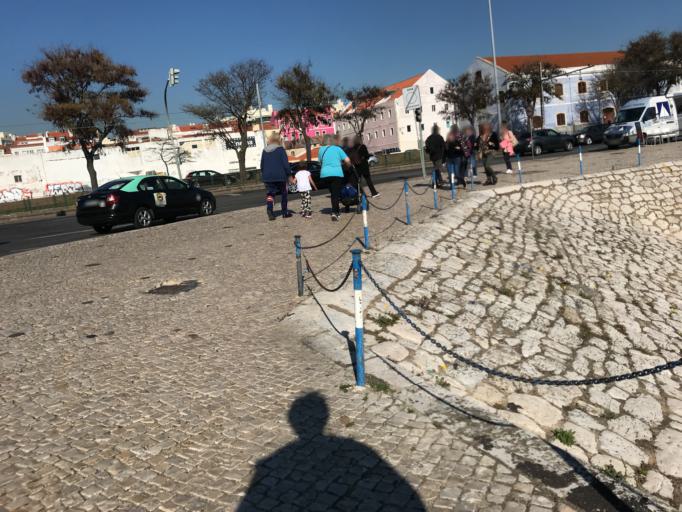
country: PT
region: Lisbon
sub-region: Oeiras
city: Alges
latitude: 38.6935
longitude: -9.2131
